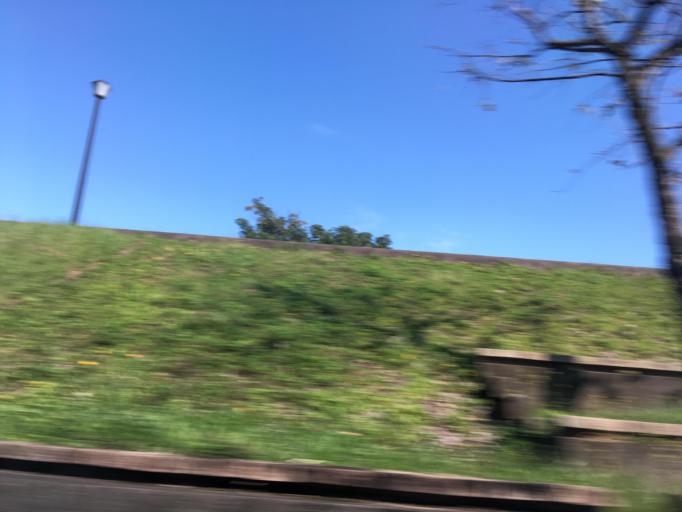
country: TW
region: Taiwan
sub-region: Yilan
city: Yilan
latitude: 24.7568
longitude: 121.7403
